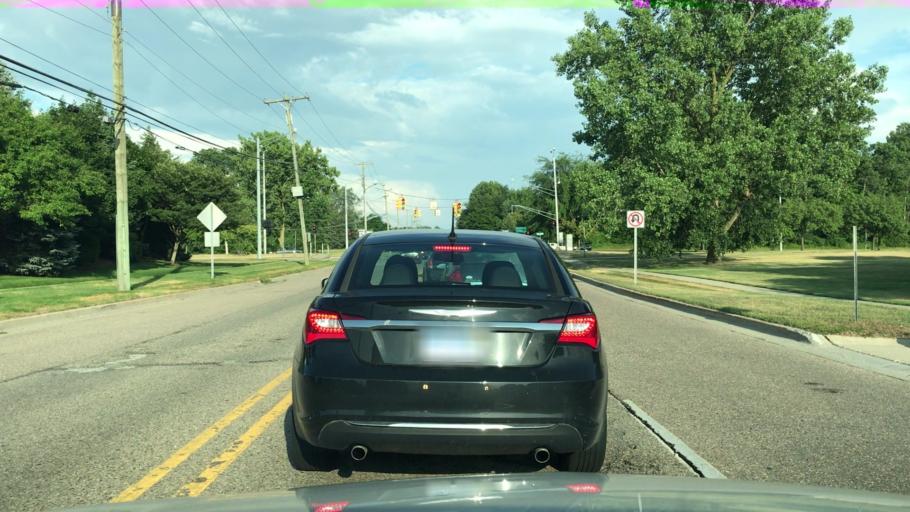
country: US
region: Michigan
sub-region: Macomb County
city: Sterling Heights
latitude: 42.5889
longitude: -82.9929
